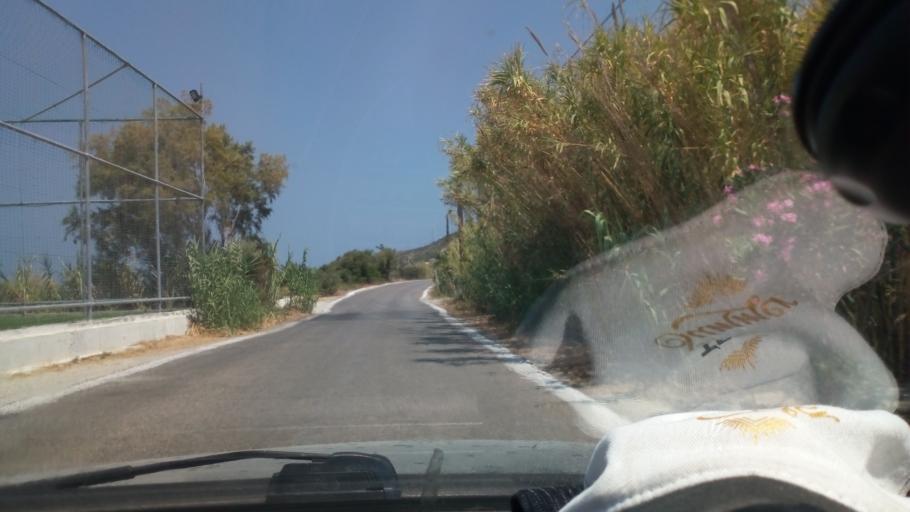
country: GR
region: North Aegean
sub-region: Nomos Samou
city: Agios Kirykos
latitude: 37.6308
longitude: 26.1076
